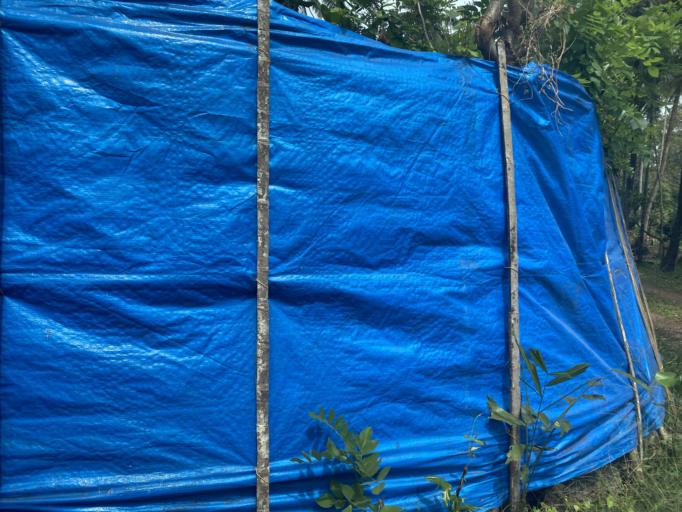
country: IN
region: Kerala
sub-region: Ernakulam
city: Elur
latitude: 10.0631
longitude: 76.2171
